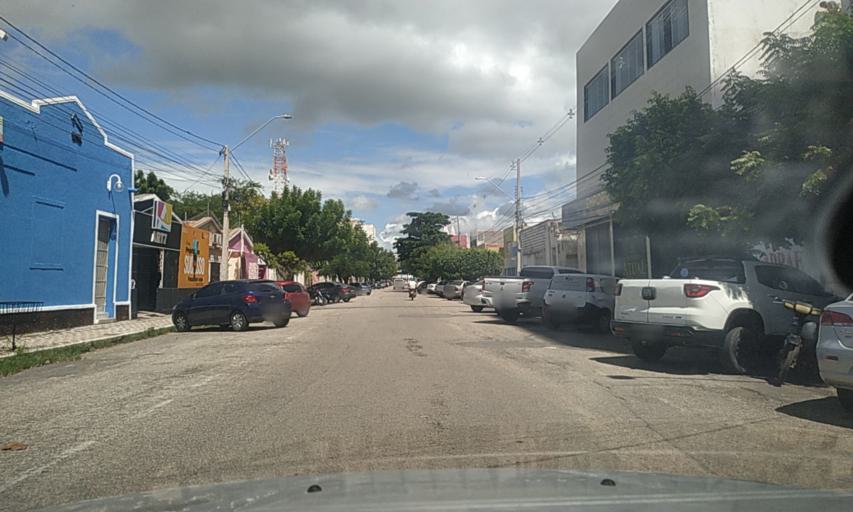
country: BR
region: Rio Grande do Norte
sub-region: Mossoro
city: Mossoro
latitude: -5.1905
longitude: -37.3391
